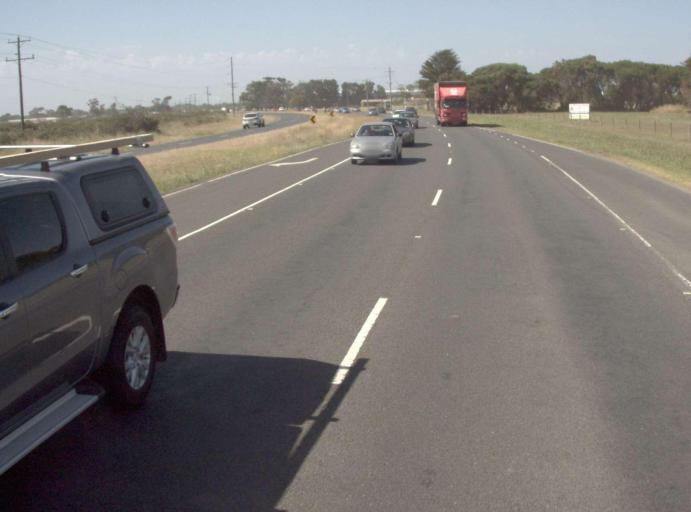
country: AU
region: Victoria
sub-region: Frankston
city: Sandhurst
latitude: -38.0583
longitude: 145.2062
